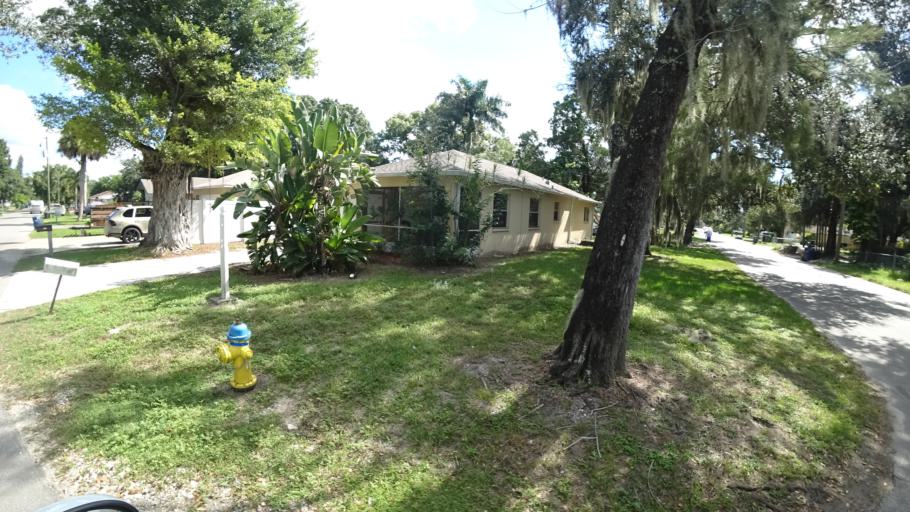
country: US
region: Florida
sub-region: Manatee County
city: West Samoset
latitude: 27.4756
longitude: -82.5687
